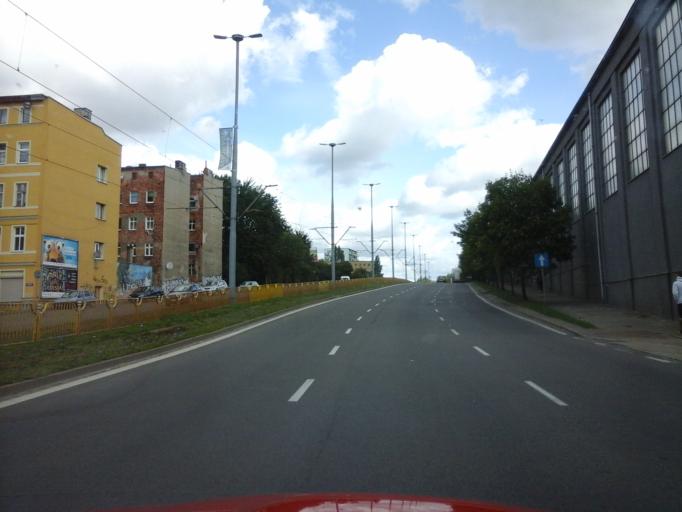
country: PL
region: West Pomeranian Voivodeship
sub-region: Szczecin
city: Szczecin
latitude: 53.4347
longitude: 14.5732
